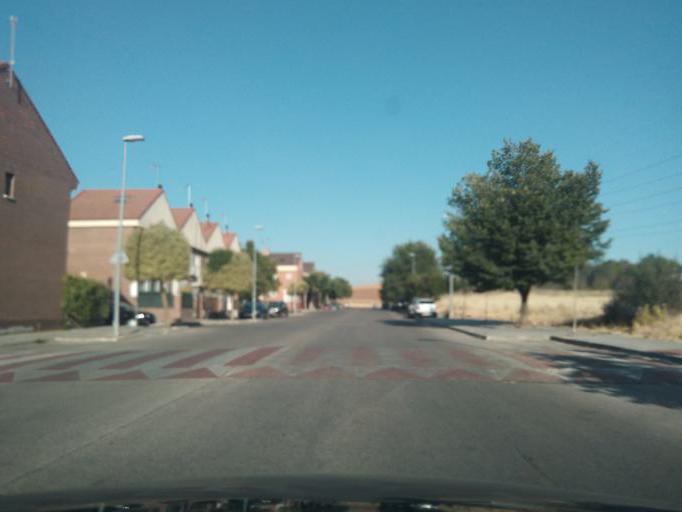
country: ES
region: Madrid
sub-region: Provincia de Madrid
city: Daganzo de Arriba
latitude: 40.5529
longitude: -3.4579
